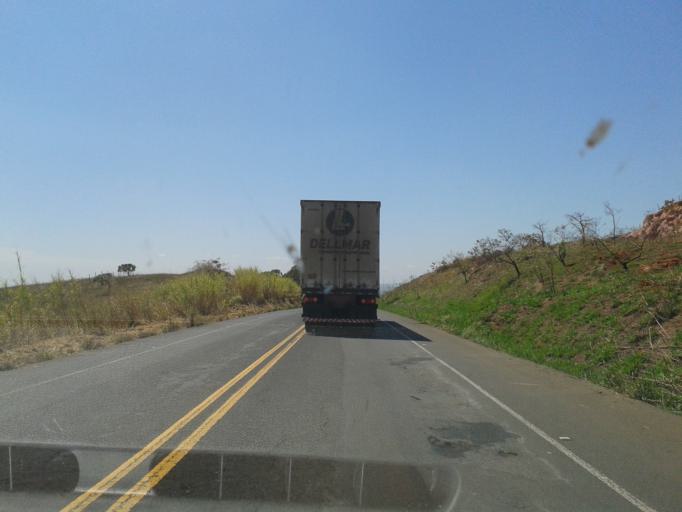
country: BR
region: Minas Gerais
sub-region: Araxa
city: Araxa
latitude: -19.4240
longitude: -47.2413
